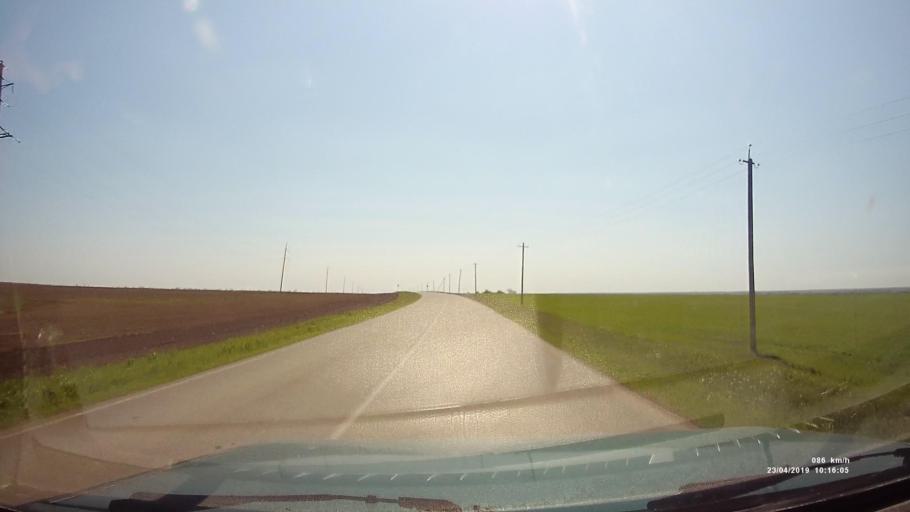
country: RU
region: Rostov
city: Sovetskoye
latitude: 46.6614
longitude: 42.3889
